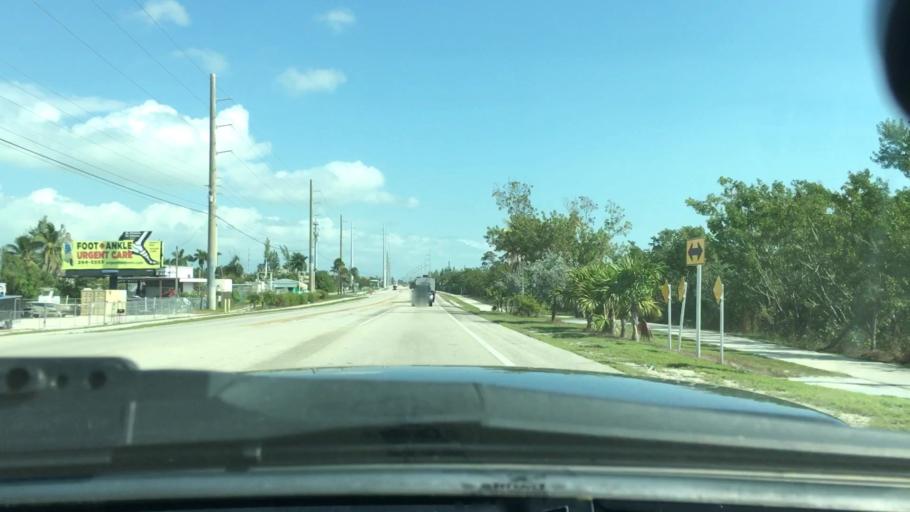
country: US
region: Florida
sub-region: Monroe County
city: Big Coppitt Key
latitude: 24.5936
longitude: -81.6642
